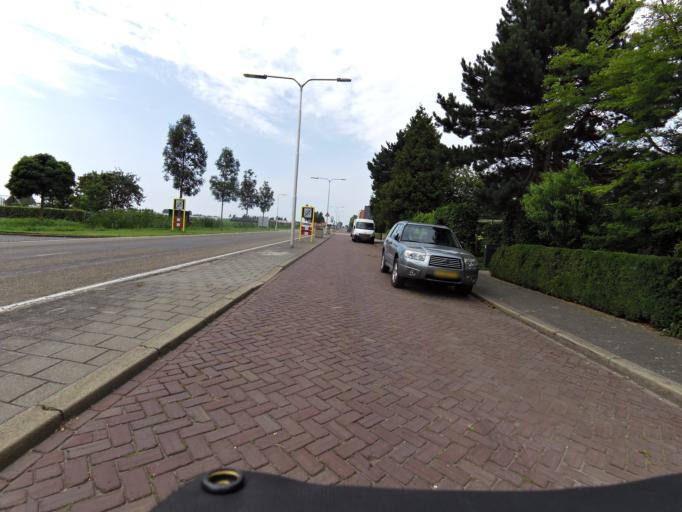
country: NL
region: North Brabant
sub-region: Gemeente Steenbergen
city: Dinteloord
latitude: 51.6840
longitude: 4.3423
